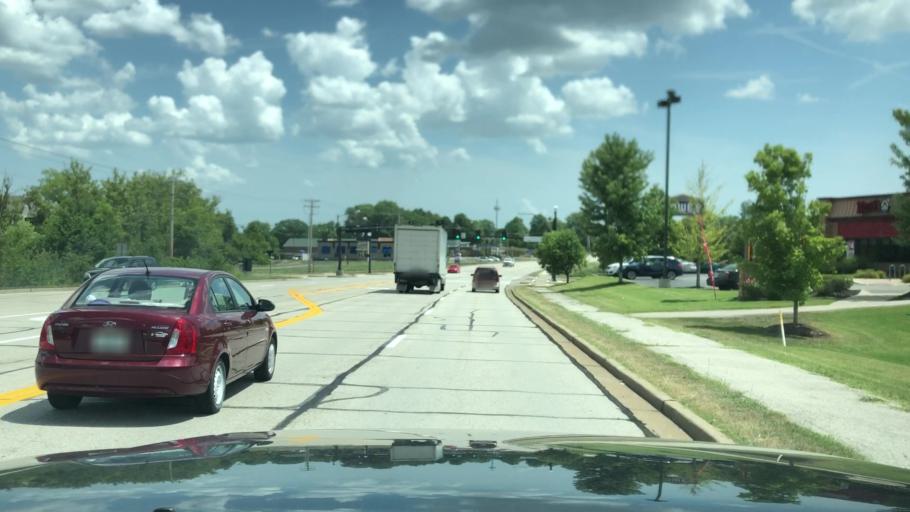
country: US
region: Missouri
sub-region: Saint Charles County
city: O'Fallon
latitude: 38.7922
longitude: -90.6976
